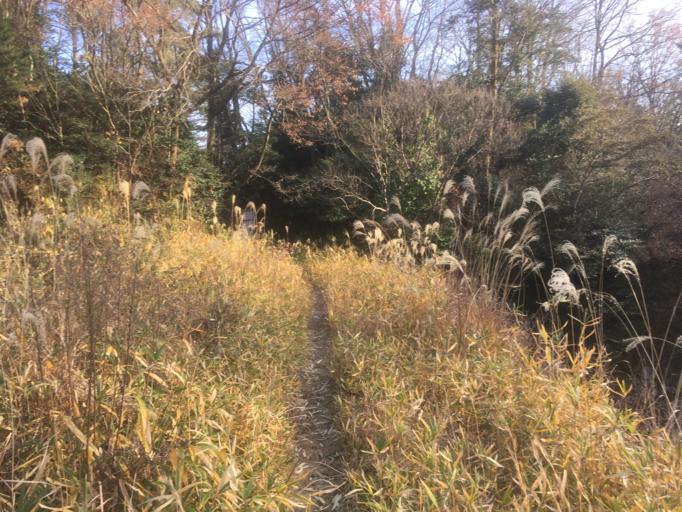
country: JP
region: Nara
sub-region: Ikoma-shi
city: Ikoma
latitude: 34.6987
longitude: 135.6798
